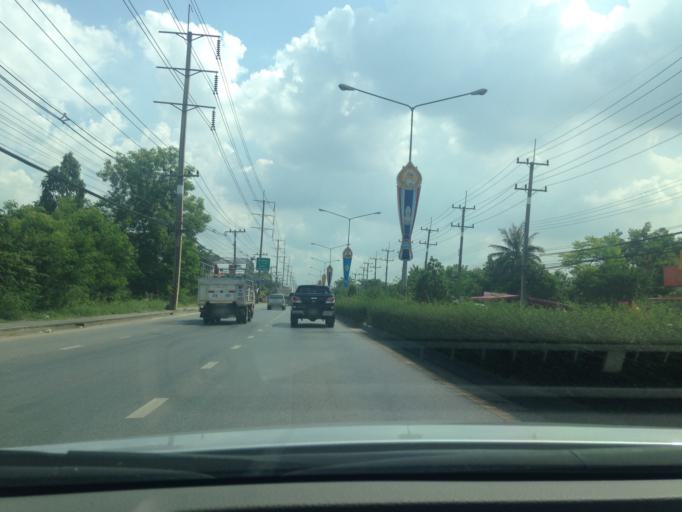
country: TH
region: Pathum Thani
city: Sam Khok
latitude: 14.0570
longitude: 100.5241
